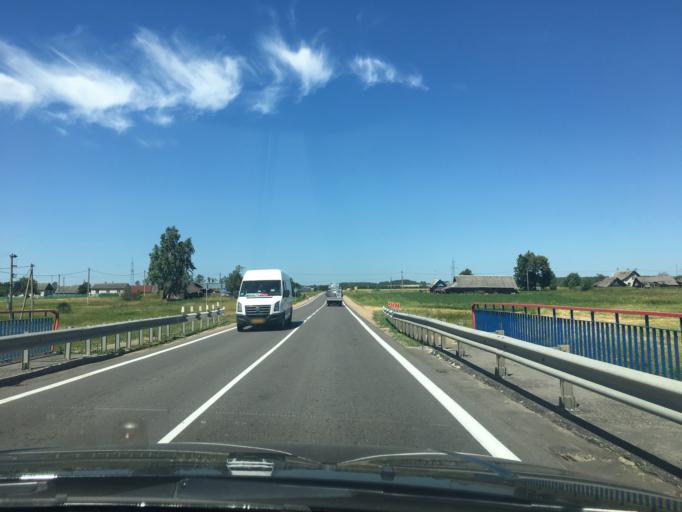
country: BY
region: Grodnenskaya
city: Hal'shany
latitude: 54.0998
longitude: 25.9154
